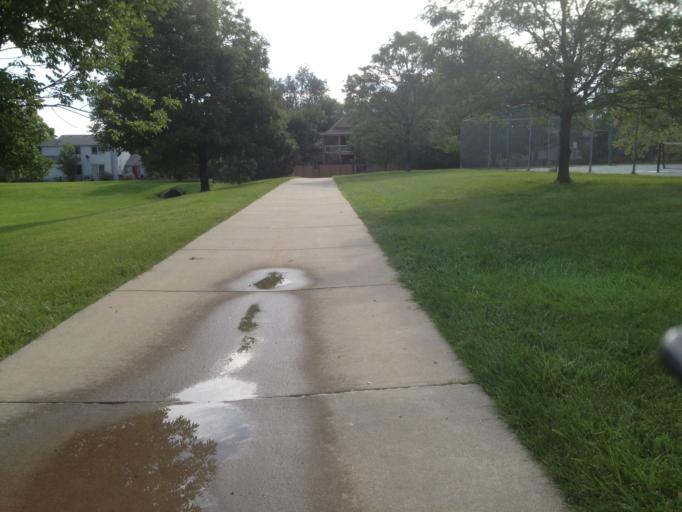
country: US
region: Colorado
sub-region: Boulder County
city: Louisville
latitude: 39.9704
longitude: -105.1406
